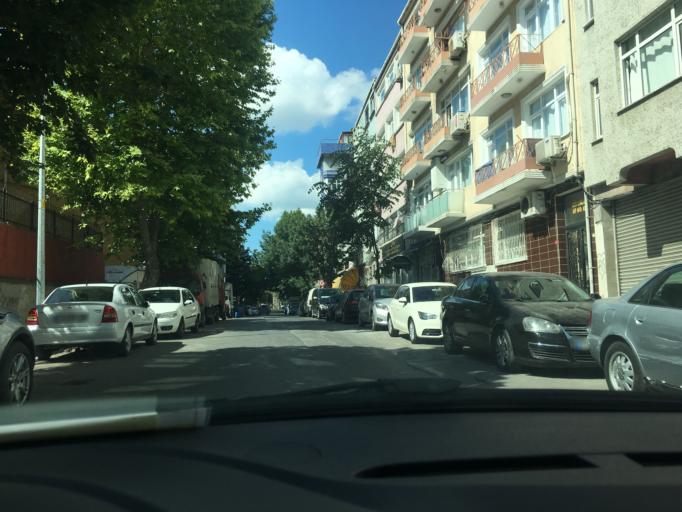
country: TR
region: Istanbul
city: Istanbul
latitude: 41.0186
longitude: 28.9547
